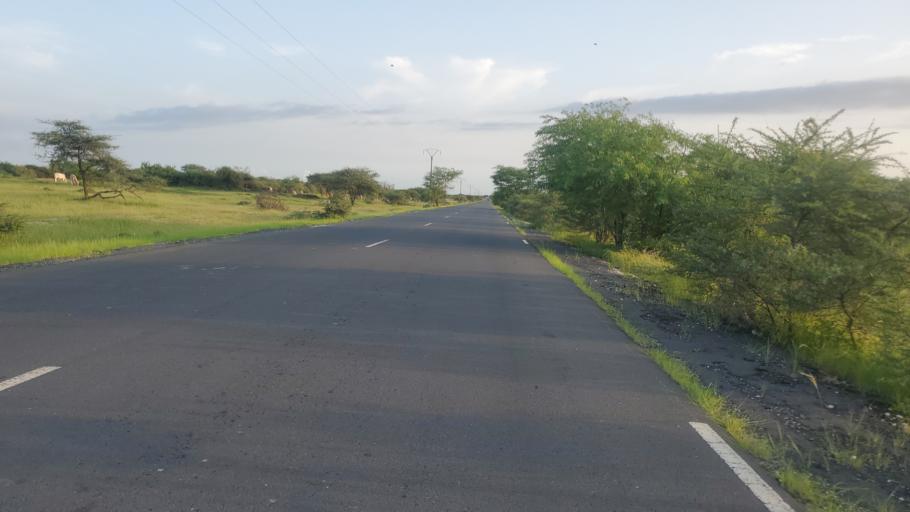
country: SN
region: Saint-Louis
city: Saint-Louis
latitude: 16.1729
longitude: -16.4098
